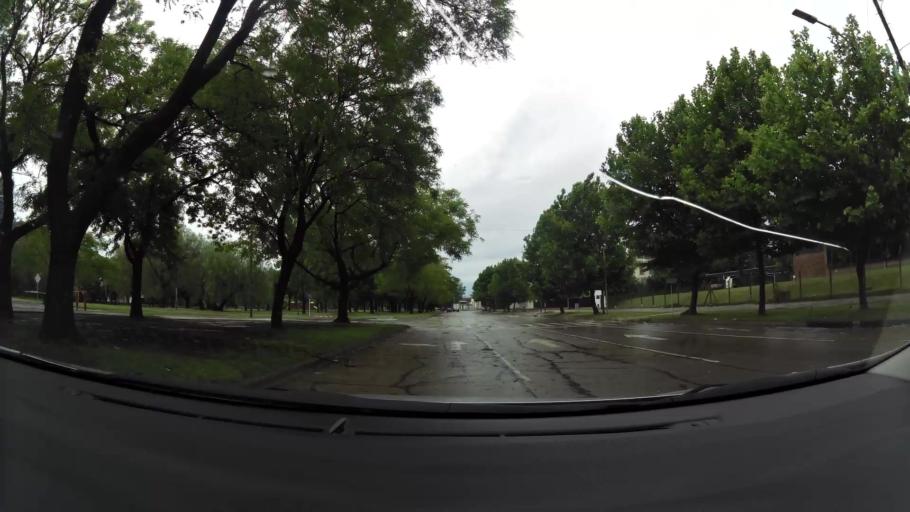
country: AR
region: Buenos Aires F.D.
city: Villa Lugano
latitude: -34.6646
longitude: -58.4369
